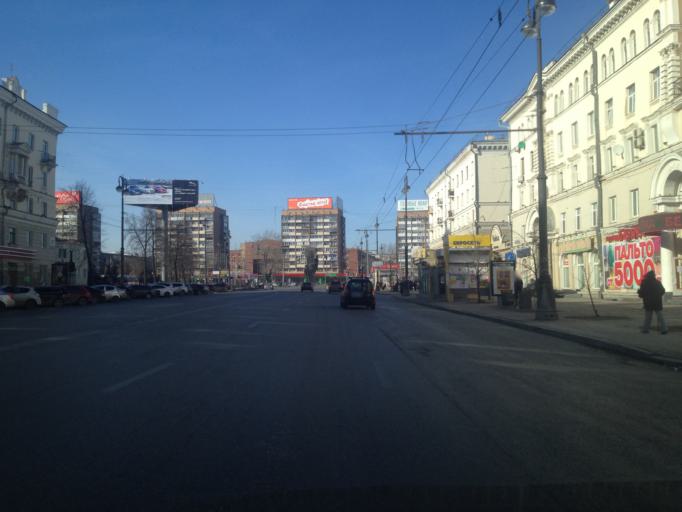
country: RU
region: Sverdlovsk
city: Yekaterinburg
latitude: 56.8543
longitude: 60.6047
